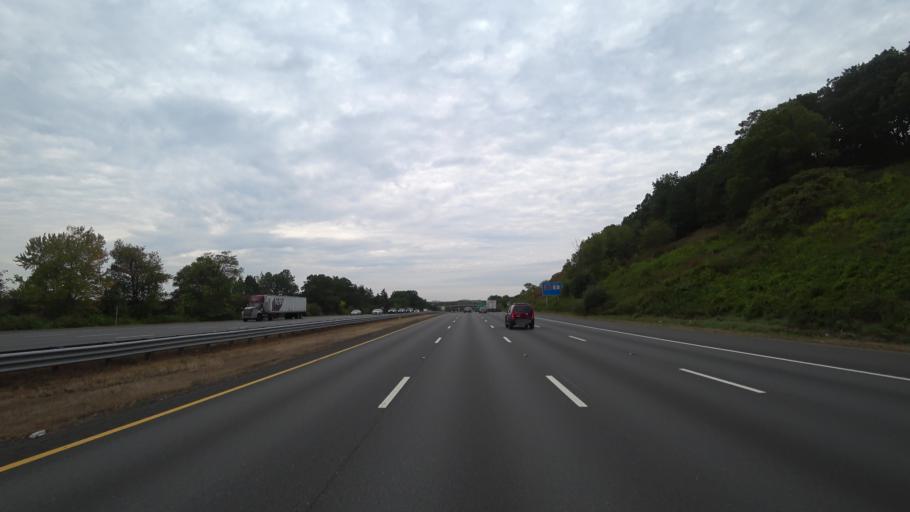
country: US
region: Massachusetts
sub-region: Middlesex County
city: Reading
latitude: 42.5137
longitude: -71.1276
